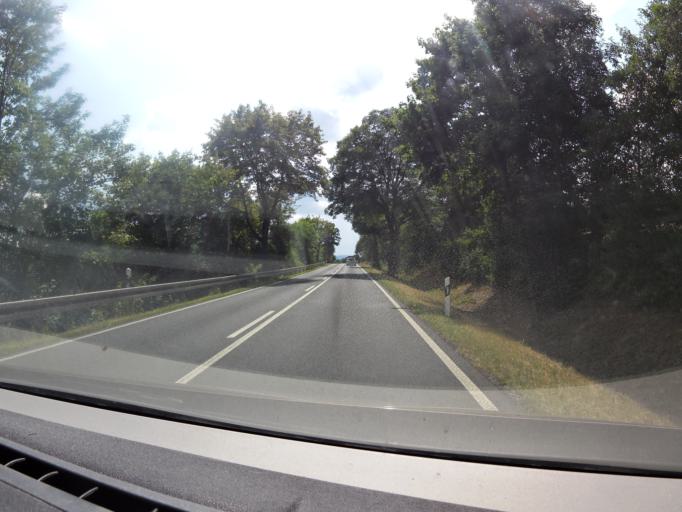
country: DE
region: Thuringia
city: Plaue
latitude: 50.7892
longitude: 10.9076
